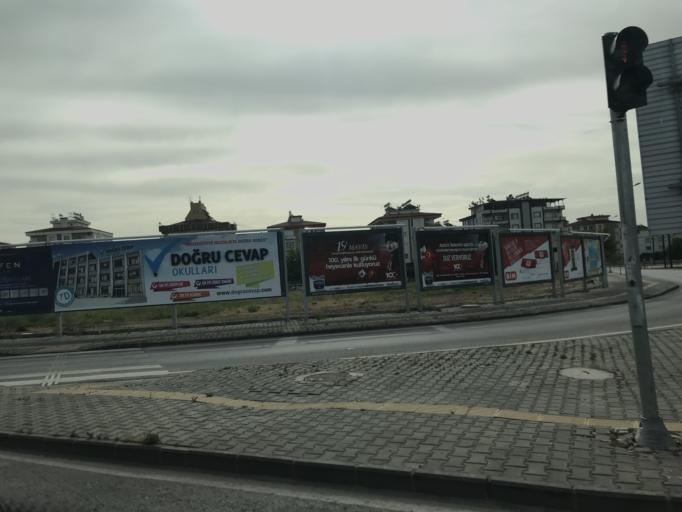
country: TR
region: Gaziantep
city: Sahinbey
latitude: 37.0688
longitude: 37.3383
